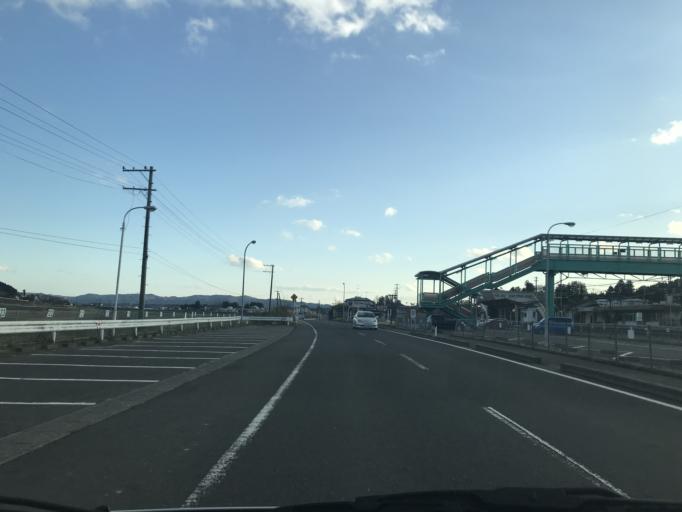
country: JP
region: Miyagi
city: Kogota
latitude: 38.6562
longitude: 141.0742
